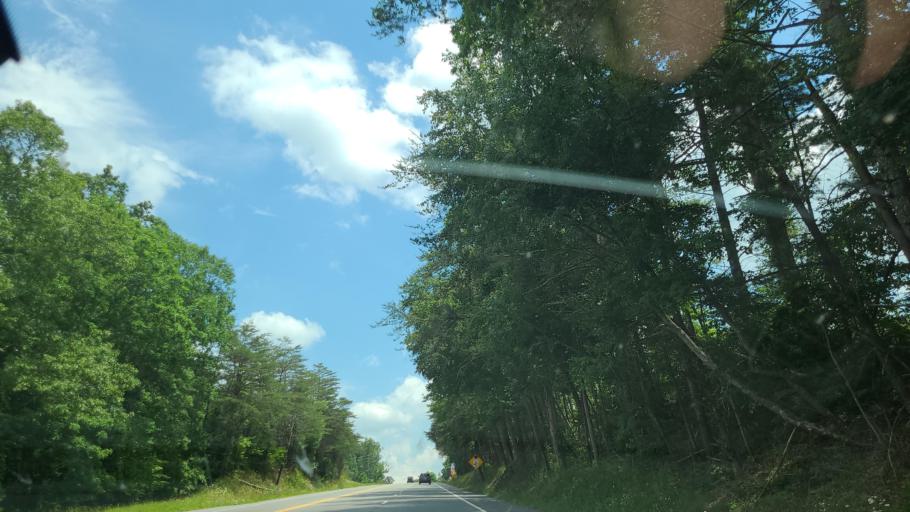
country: US
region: Tennessee
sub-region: Cumberland County
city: Crossville
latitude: 35.9092
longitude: -84.9894
